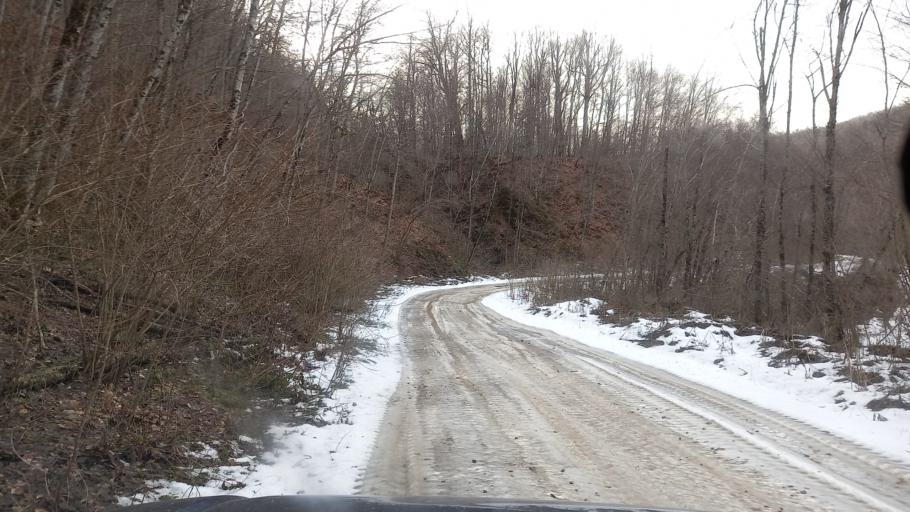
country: RU
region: Adygeya
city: Kamennomostskiy
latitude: 44.1534
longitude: 40.3016
